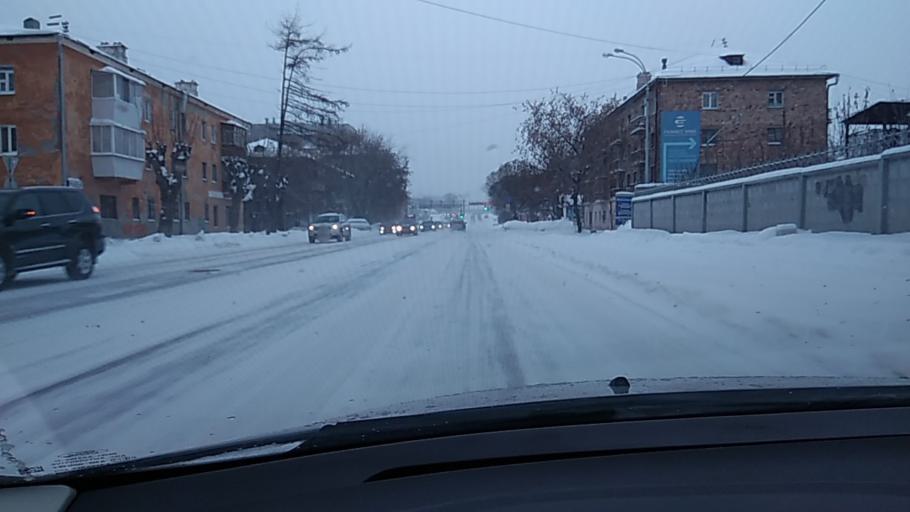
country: RU
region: Sverdlovsk
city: Yekaterinburg
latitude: 56.8252
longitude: 60.5709
